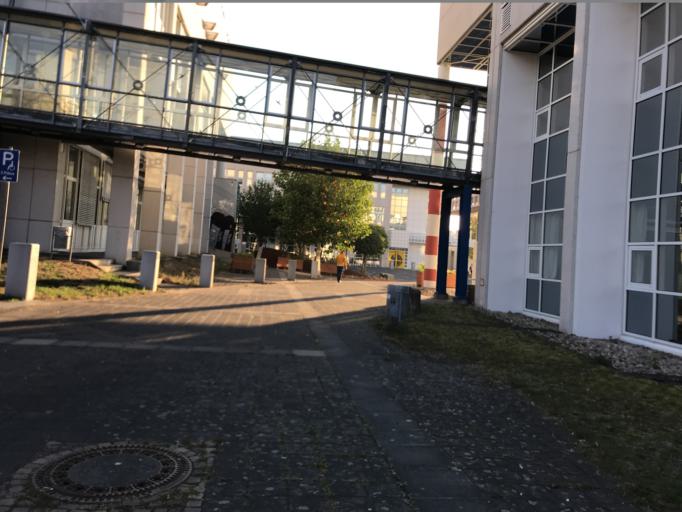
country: DE
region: Rheinland-Pfalz
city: Munster-Sarmsheim
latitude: 49.9528
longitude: 7.9242
